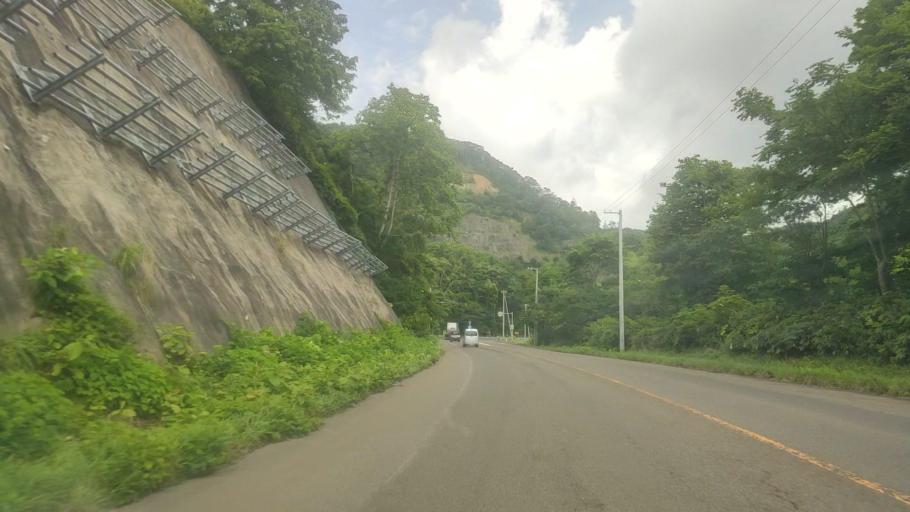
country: JP
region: Hokkaido
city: Niseko Town
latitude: 42.5968
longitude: 140.4602
